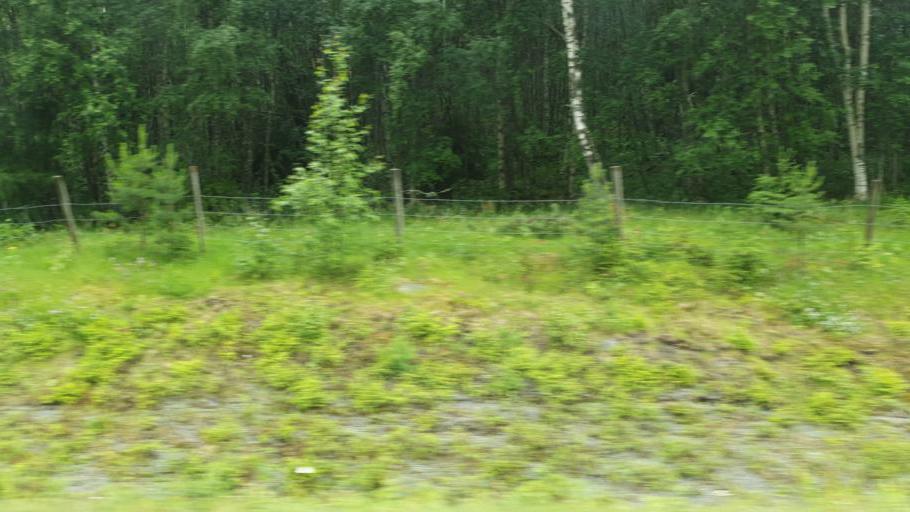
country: NO
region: Oppland
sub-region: Dovre
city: Dovre
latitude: 61.8545
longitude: 9.2697
